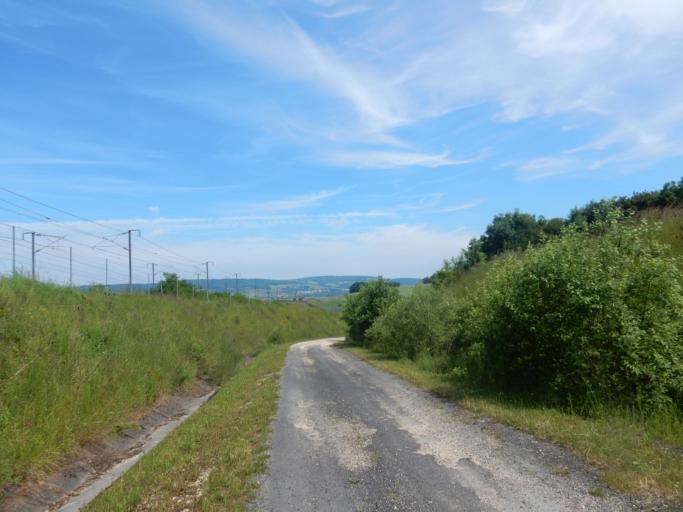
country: FR
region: Lorraine
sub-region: Departement de Meurthe-et-Moselle
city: Pagny-sur-Moselle
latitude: 48.9722
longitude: 5.9864
